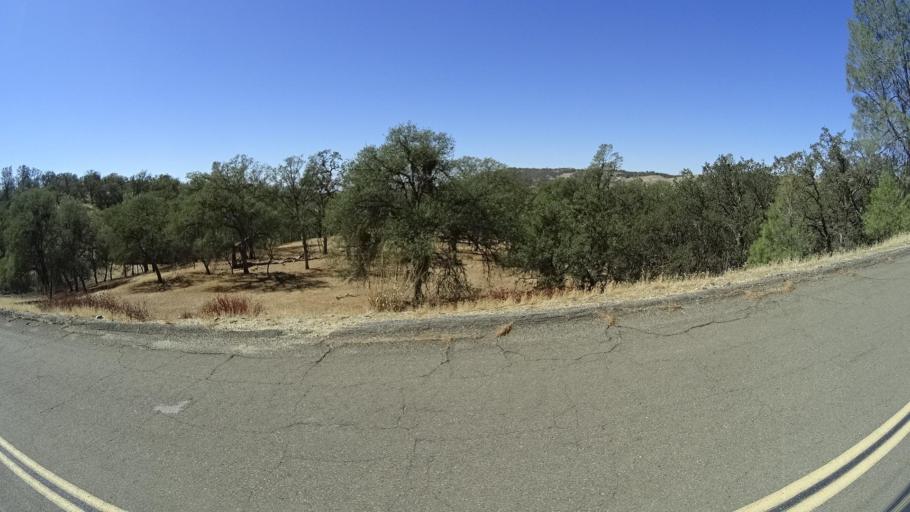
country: US
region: California
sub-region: San Luis Obispo County
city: San Miguel
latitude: 35.9199
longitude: -120.5336
